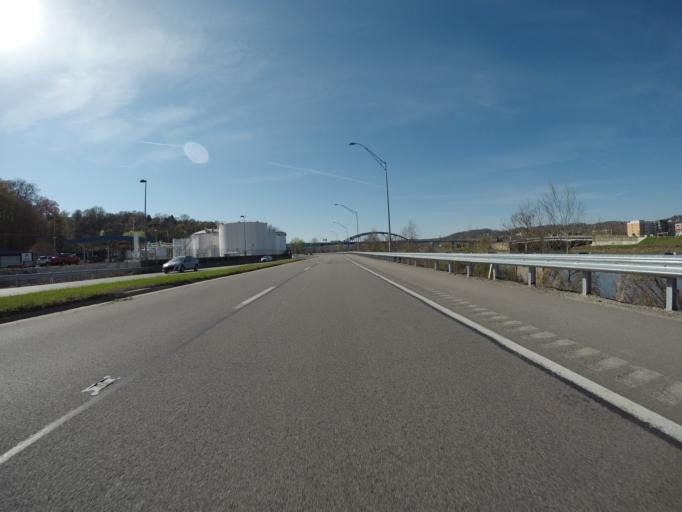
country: US
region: West Virginia
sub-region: Kanawha County
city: Charleston
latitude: 38.3513
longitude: -81.6443
